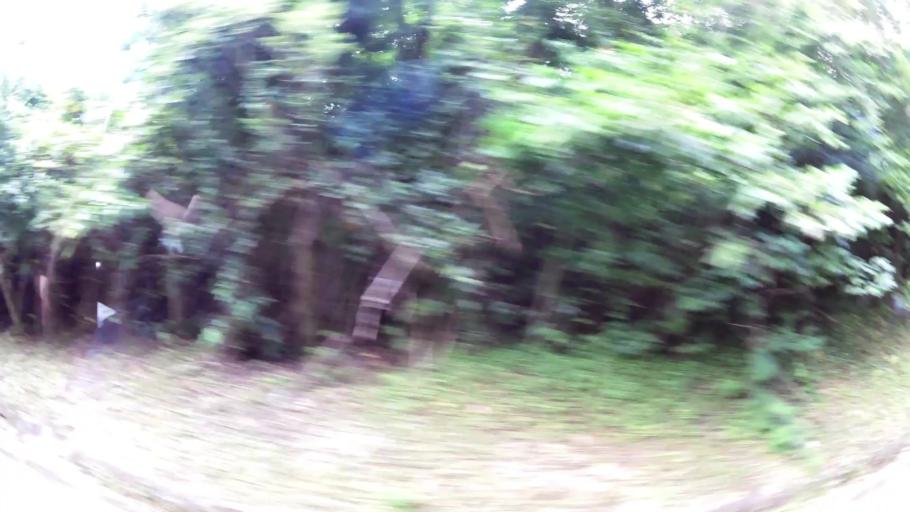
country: MQ
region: Martinique
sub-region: Martinique
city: Les Trois-Ilets
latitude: 14.5131
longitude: -61.0749
